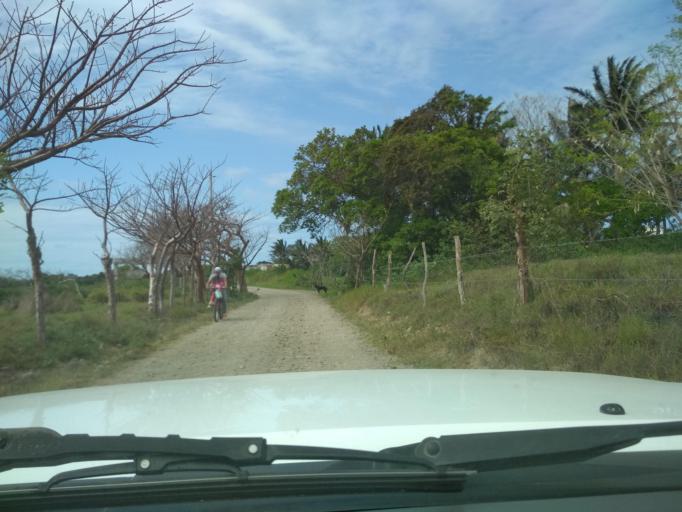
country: MX
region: Veracruz
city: Anton Lizardo
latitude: 19.0276
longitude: -95.9690
